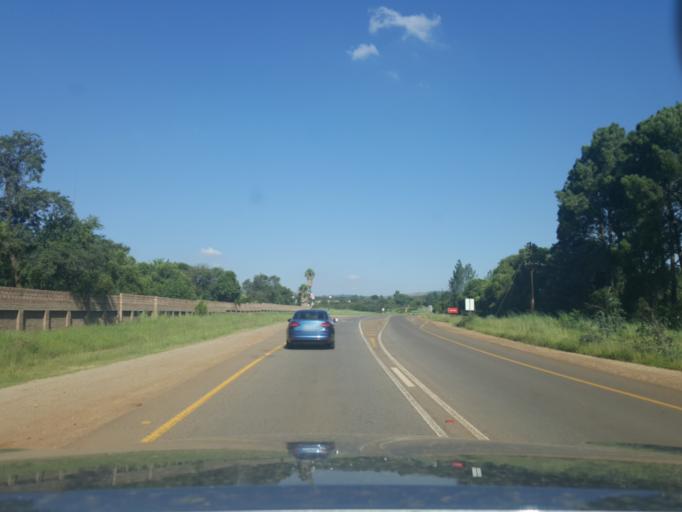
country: ZA
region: Gauteng
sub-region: City of Tshwane Metropolitan Municipality
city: Cullinan
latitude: -25.7611
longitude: 28.4176
